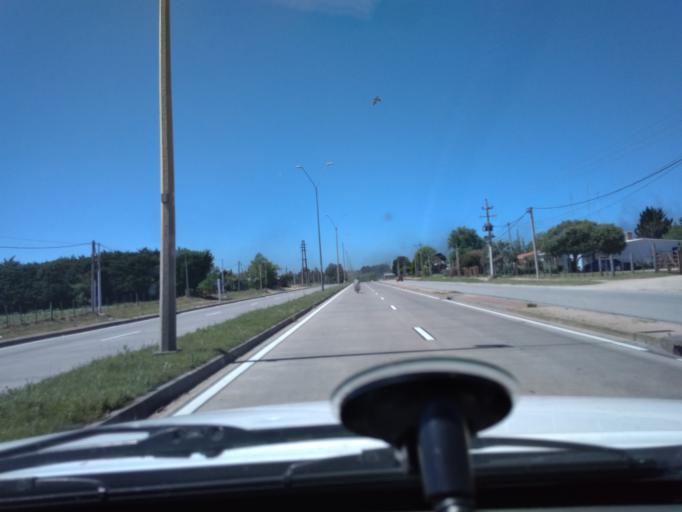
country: UY
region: Canelones
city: Toledo
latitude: -34.7930
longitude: -56.1159
